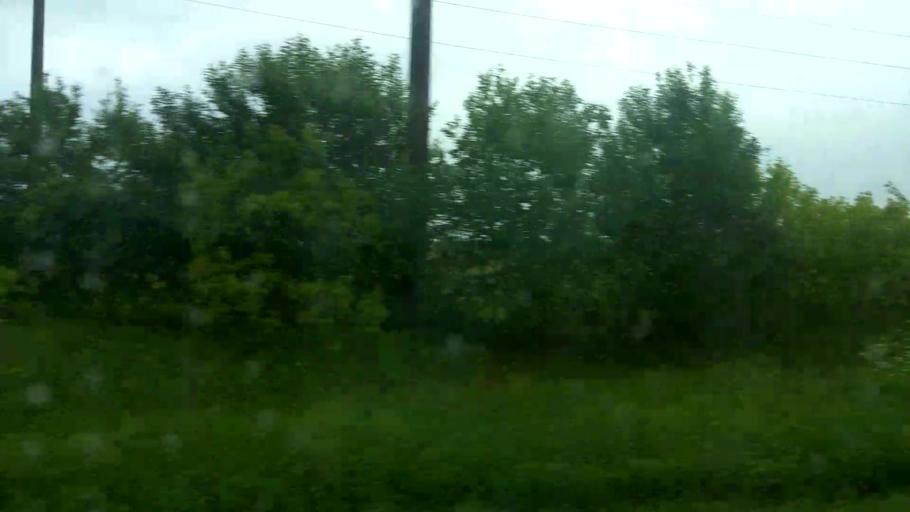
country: RU
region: Moskovskaya
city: Ozherel'ye
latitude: 54.8480
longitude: 38.2654
